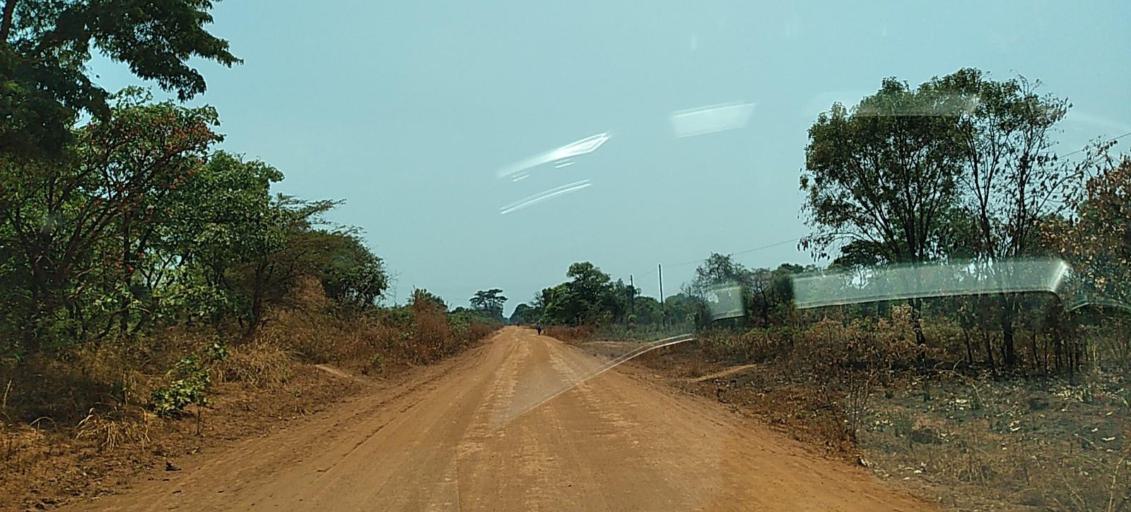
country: CD
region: Katanga
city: Kipushi
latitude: -11.9679
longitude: 26.9015
